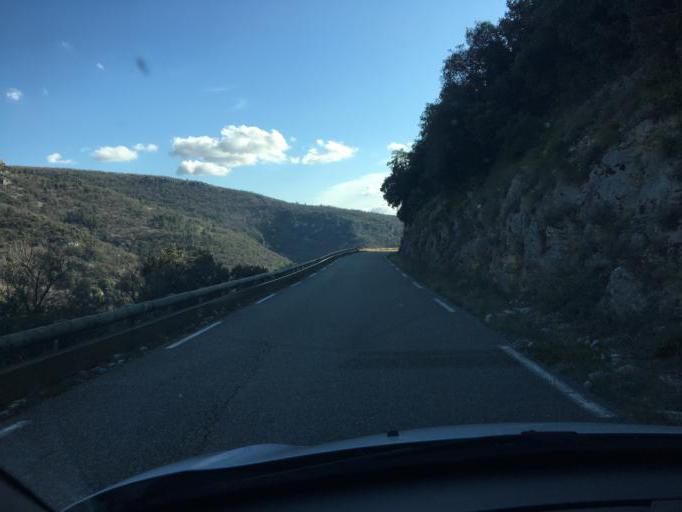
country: FR
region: Provence-Alpes-Cote d'Azur
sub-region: Departement du Vaucluse
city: Villes-sur-Auzon
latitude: 44.0602
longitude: 5.3013
